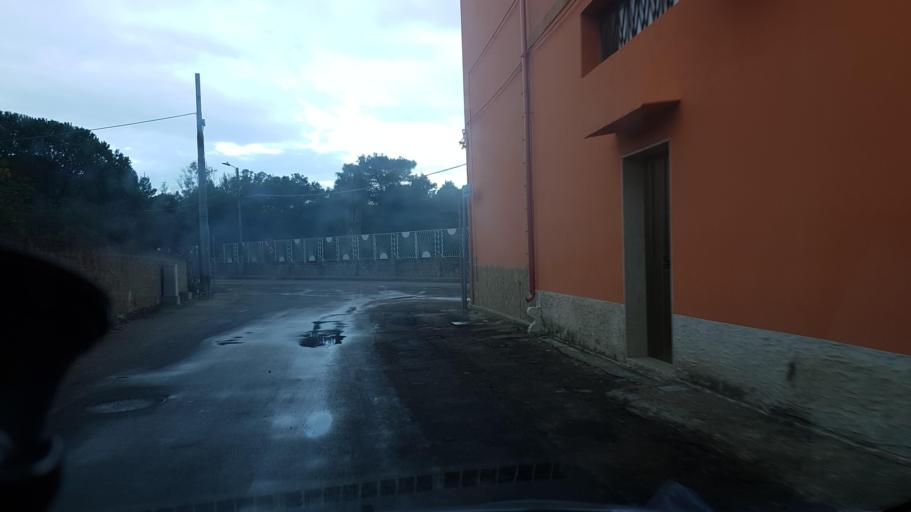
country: IT
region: Apulia
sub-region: Provincia di Lecce
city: Novoli
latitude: 40.3652
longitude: 18.0724
